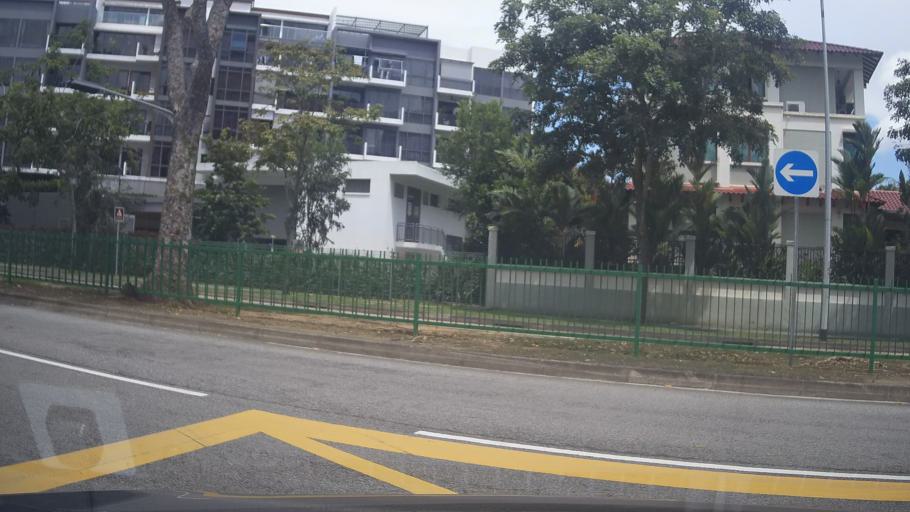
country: MY
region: Johor
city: Kampung Pasir Gudang Baru
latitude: 1.3782
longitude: 103.9434
